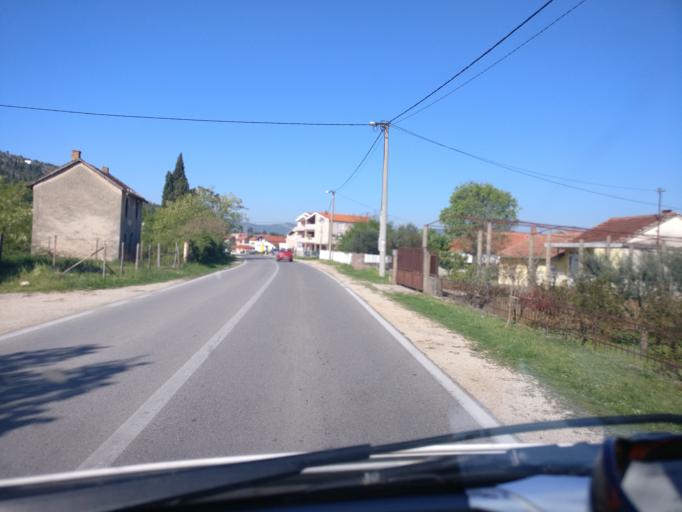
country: BA
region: Federation of Bosnia and Herzegovina
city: Tasovcici
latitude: 43.1200
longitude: 17.7418
